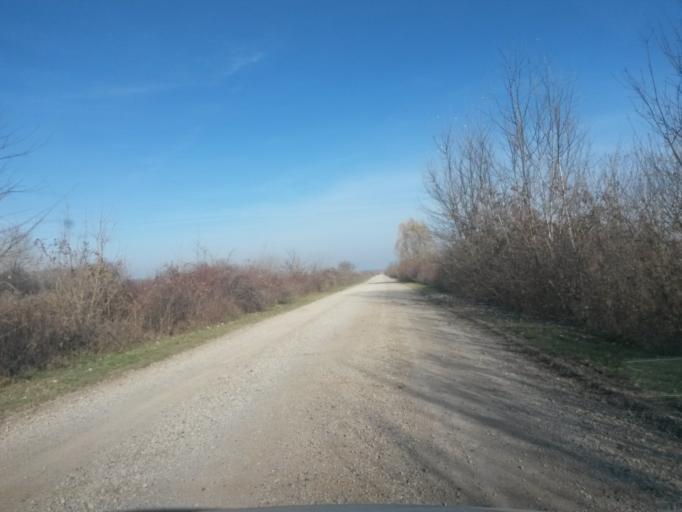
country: HR
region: Vukovarsko-Srijemska
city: Mirkovci
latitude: 45.2283
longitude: 18.8812
